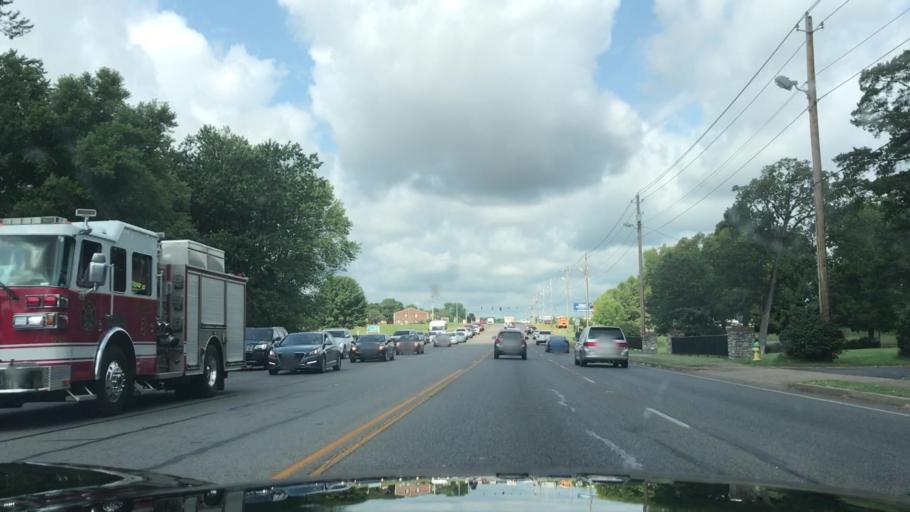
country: US
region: Kentucky
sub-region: Warren County
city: Bowling Green
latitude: 36.9608
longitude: -86.4552
